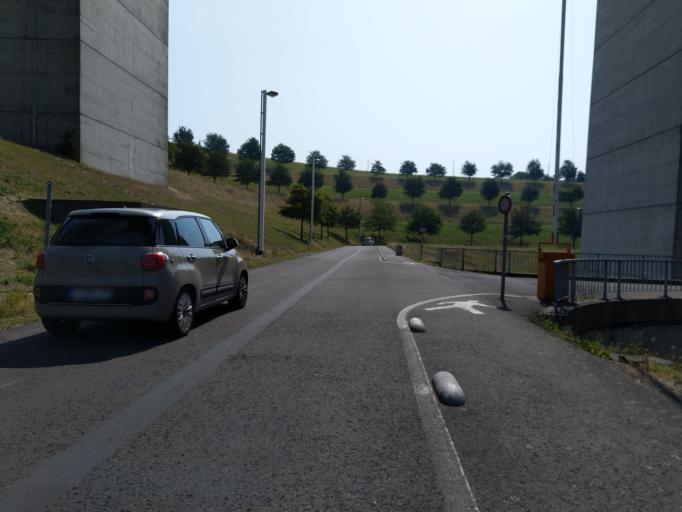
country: BE
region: Wallonia
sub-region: Province du Hainaut
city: Roeulx
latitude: 50.4795
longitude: 4.1103
